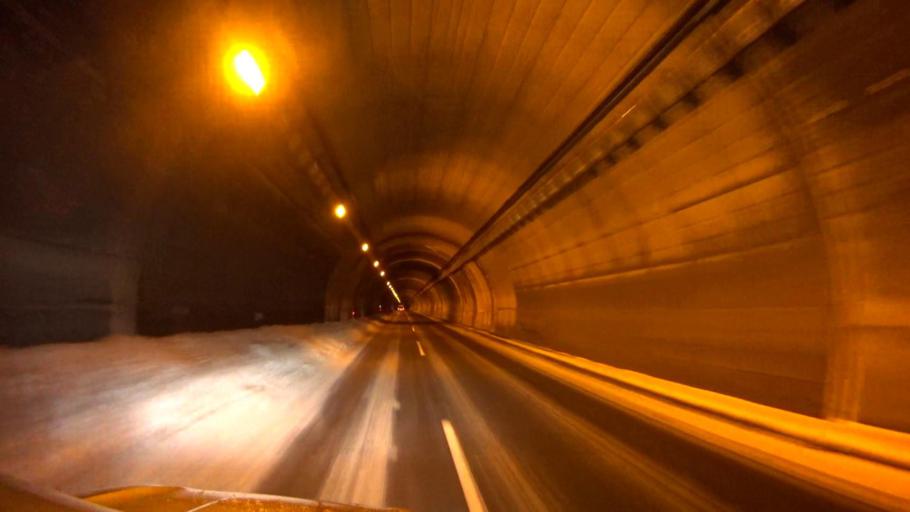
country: JP
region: Hokkaido
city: Otaru
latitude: 43.1761
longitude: 141.0268
